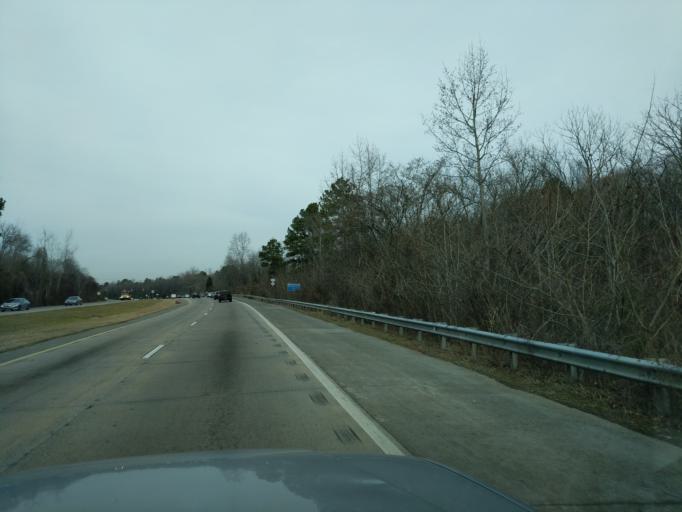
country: US
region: North Carolina
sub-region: Mecklenburg County
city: Charlotte
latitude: 35.2026
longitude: -80.9217
